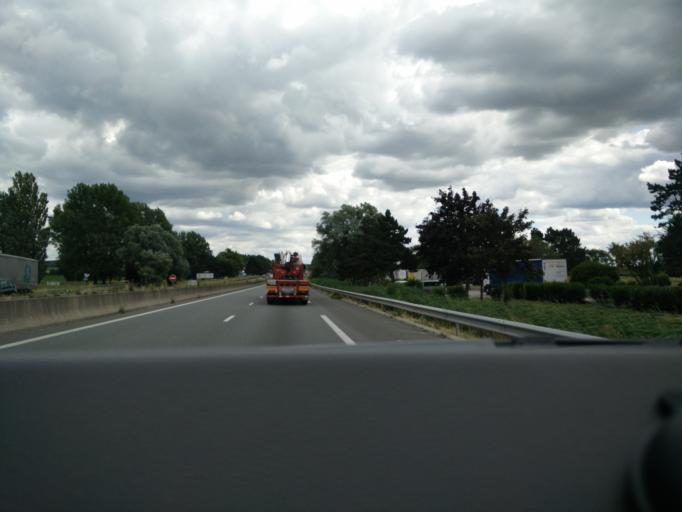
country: FR
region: Nord-Pas-de-Calais
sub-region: Departement du Nord
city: Steenvoorde
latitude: 50.8302
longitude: 2.5811
